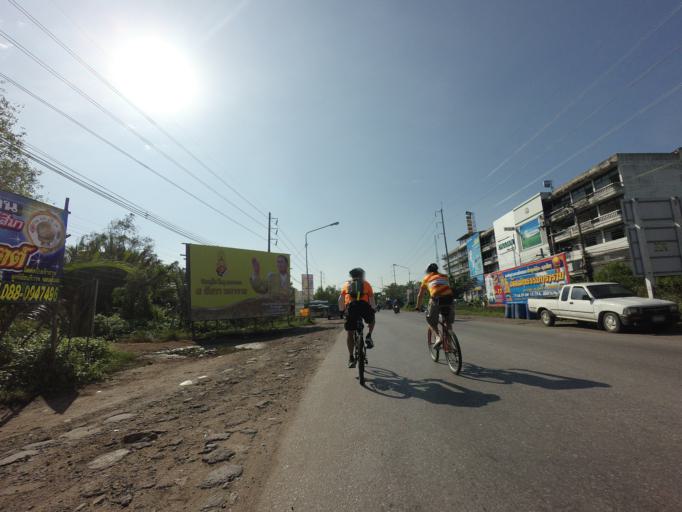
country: TH
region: Samut Prakan
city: Phra Samut Chedi
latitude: 13.5928
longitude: 100.5800
